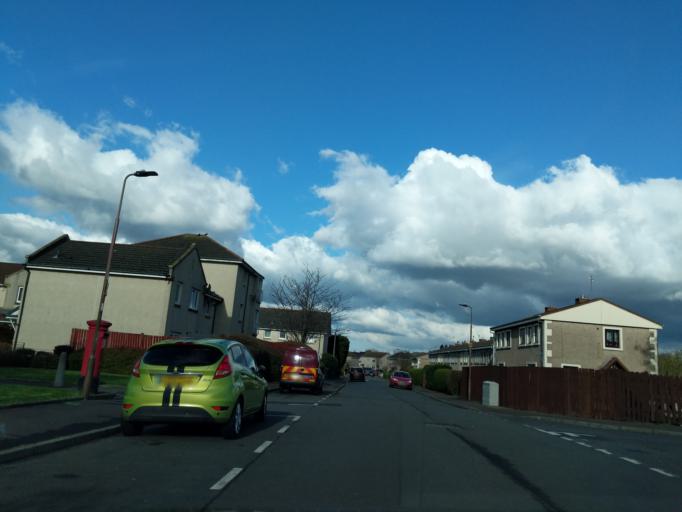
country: GB
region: Scotland
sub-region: Edinburgh
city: Colinton
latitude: 55.9292
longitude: -3.2699
